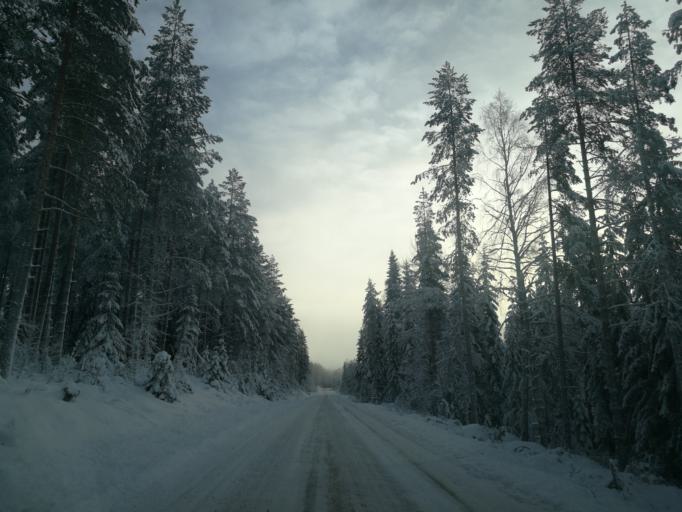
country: SE
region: Vaermland
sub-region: Torsby Kommun
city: Torsby
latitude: 60.6492
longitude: 12.7237
